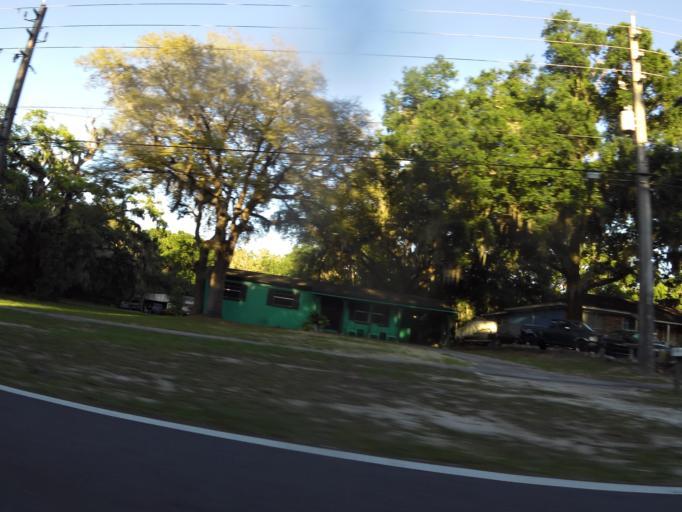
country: US
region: Florida
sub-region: Duval County
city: Atlantic Beach
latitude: 30.3623
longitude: -81.5155
